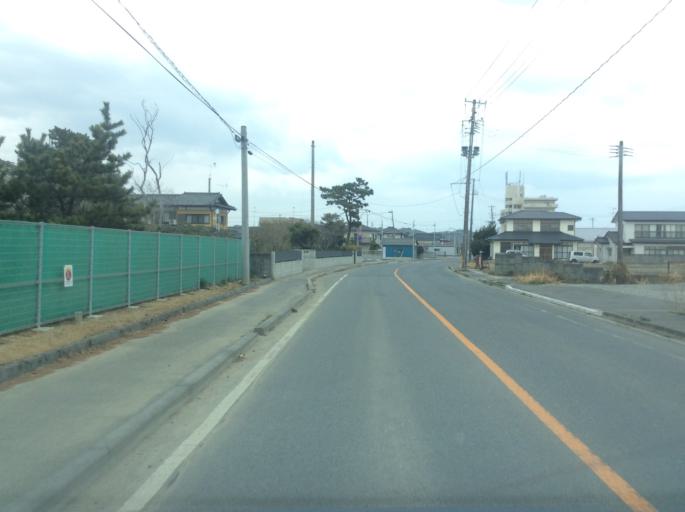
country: JP
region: Fukushima
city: Iwaki
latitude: 37.0989
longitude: 140.9858
